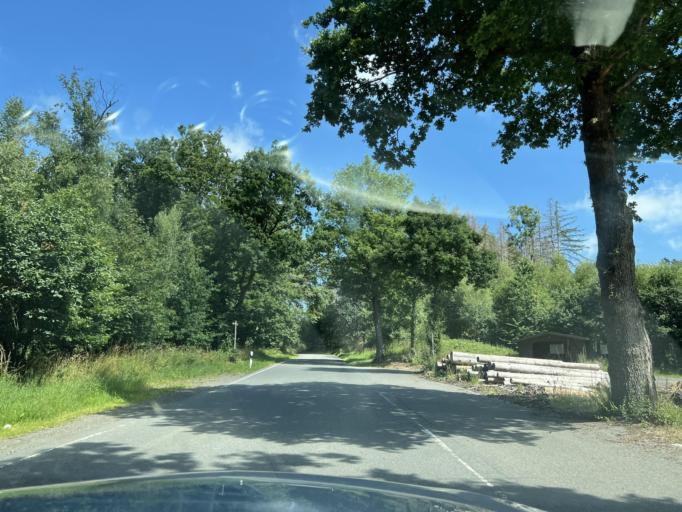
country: DE
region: North Rhine-Westphalia
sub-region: Regierungsbezirk Arnsberg
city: Drolshagen
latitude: 50.9766
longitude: 7.7316
